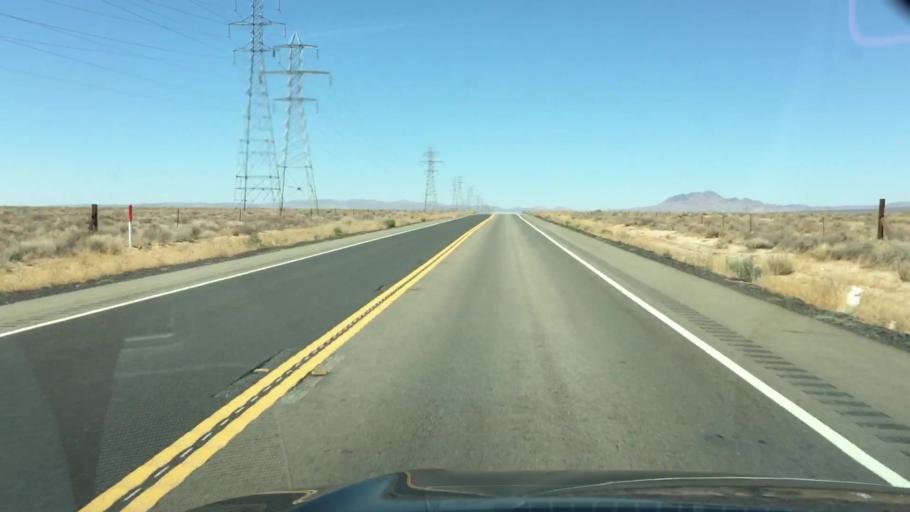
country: US
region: California
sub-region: Kern County
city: Boron
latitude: 35.1296
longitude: -117.5798
